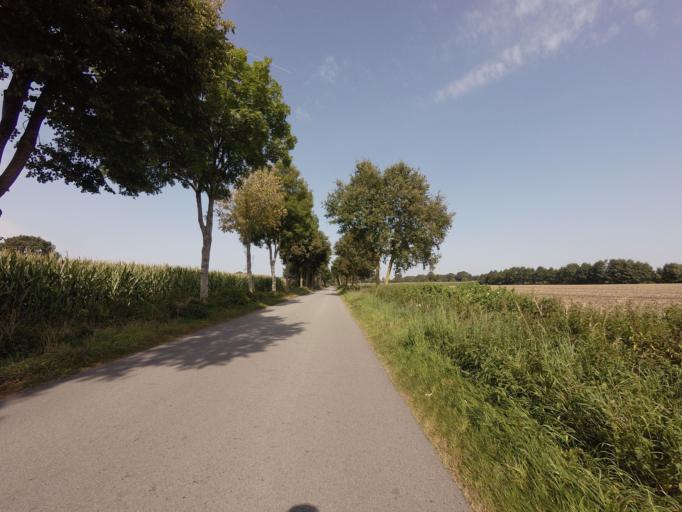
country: DE
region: Lower Saxony
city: Itterbeck
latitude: 52.5319
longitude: 6.7675
